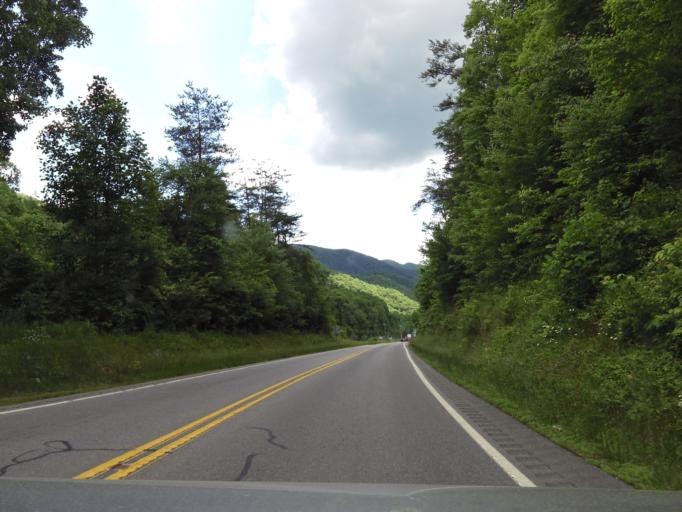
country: US
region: North Carolina
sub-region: Graham County
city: Robbinsville
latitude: 35.2511
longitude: -83.7017
